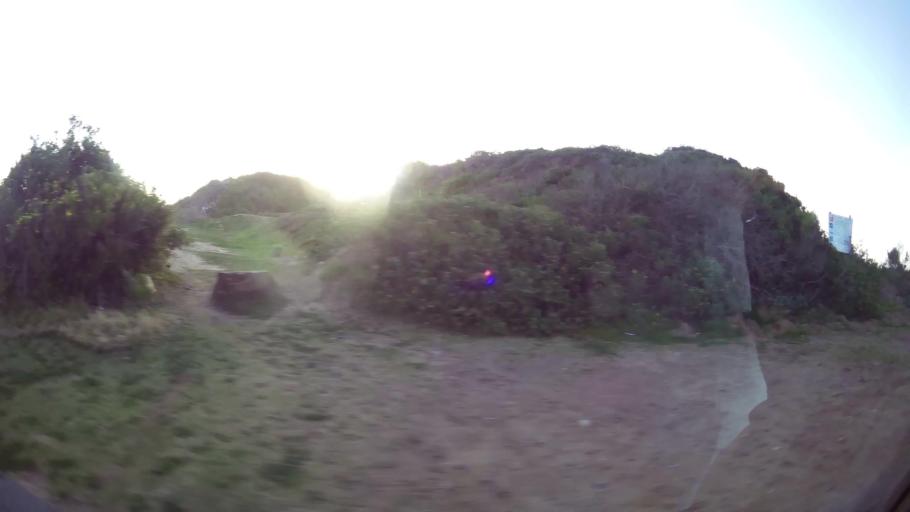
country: ZA
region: Western Cape
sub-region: Eden District Municipality
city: George
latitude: -34.0034
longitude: 22.6464
